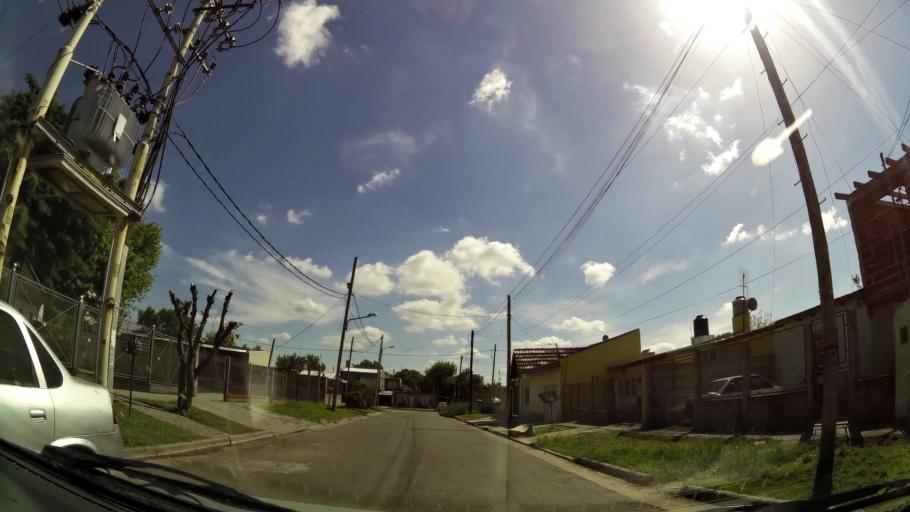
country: AR
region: Buenos Aires
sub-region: Partido de Quilmes
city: Quilmes
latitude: -34.8033
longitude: -58.2643
